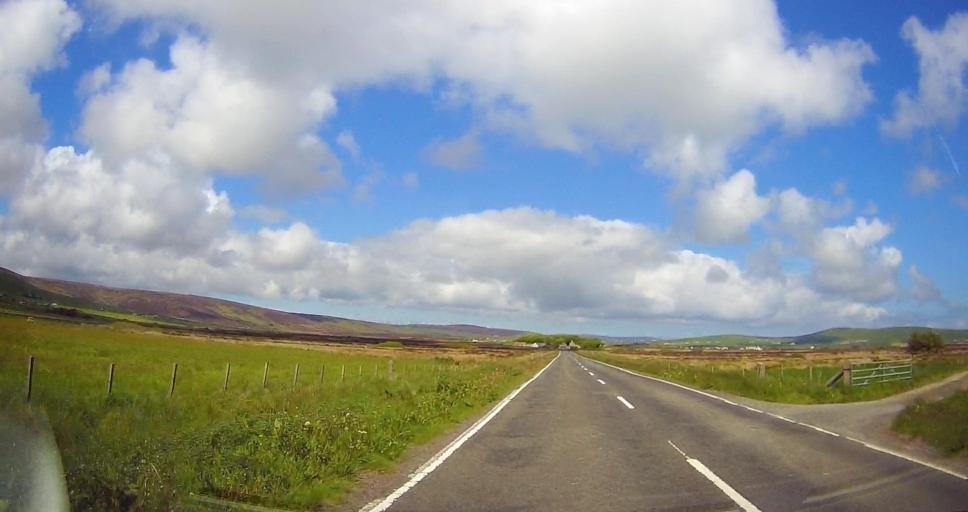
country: GB
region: Scotland
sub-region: Orkney Islands
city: Orkney
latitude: 59.0402
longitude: -3.0871
